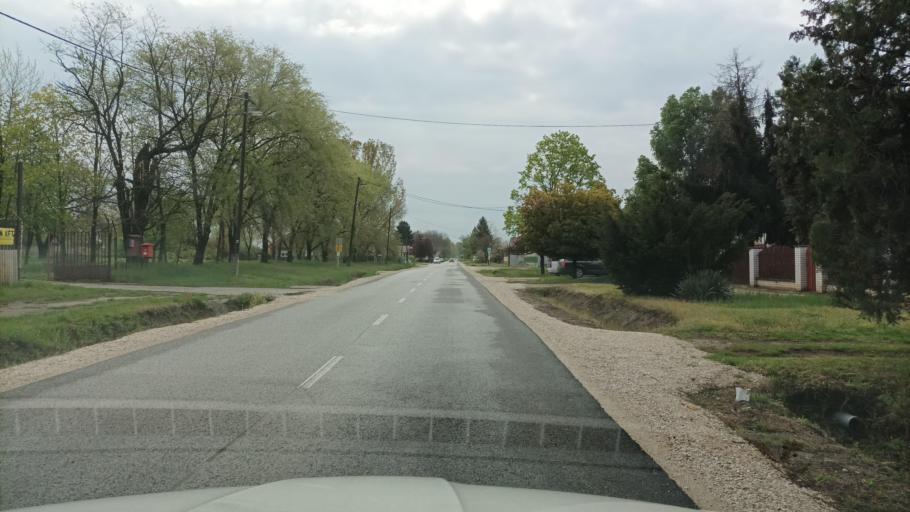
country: HU
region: Pest
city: Danszentmiklos
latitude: 47.1701
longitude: 19.5036
